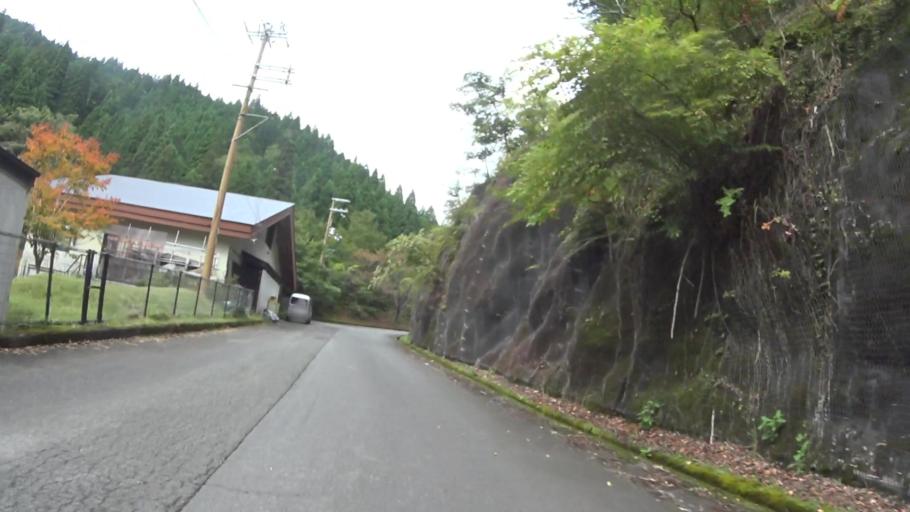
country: JP
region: Shiga Prefecture
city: Kitahama
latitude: 35.2669
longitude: 135.7415
